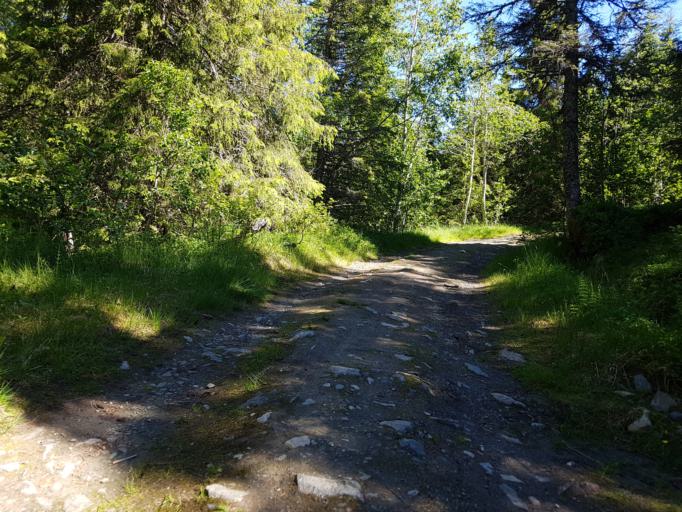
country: NO
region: Sor-Trondelag
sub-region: Melhus
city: Melhus
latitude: 63.4311
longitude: 10.2195
